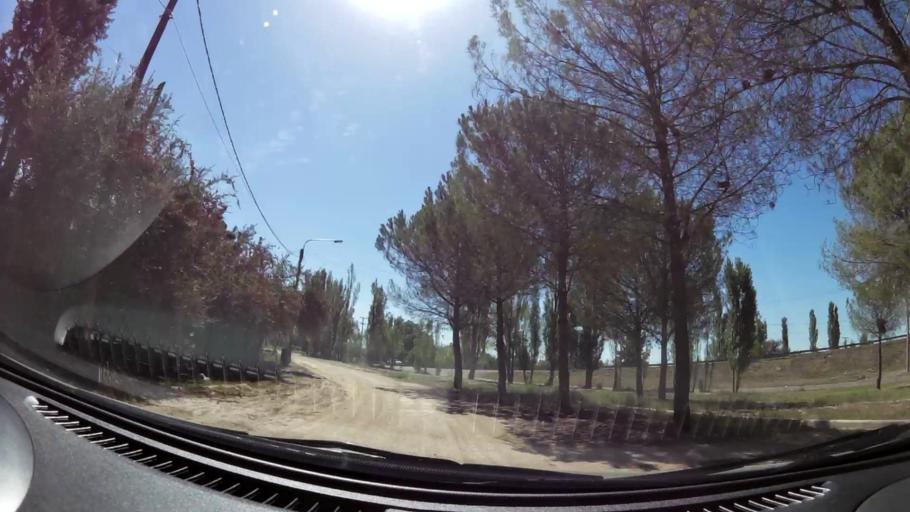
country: AR
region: Mendoza
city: Lujan de Cuyo
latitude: -32.9850
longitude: -68.8507
